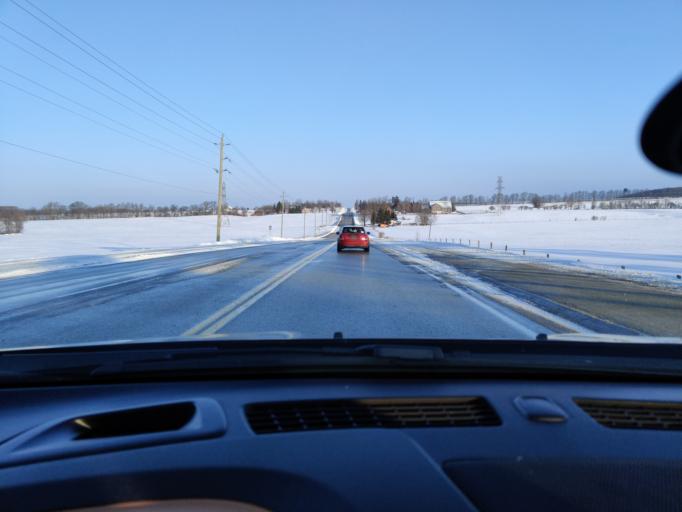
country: CA
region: Ontario
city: Angus
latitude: 44.3739
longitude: -79.7813
